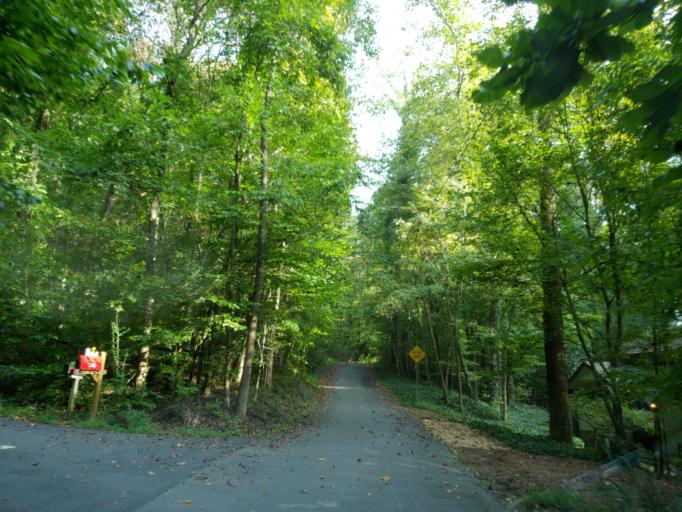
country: US
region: Georgia
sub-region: Fulton County
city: Roswell
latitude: 34.0816
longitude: -84.4138
